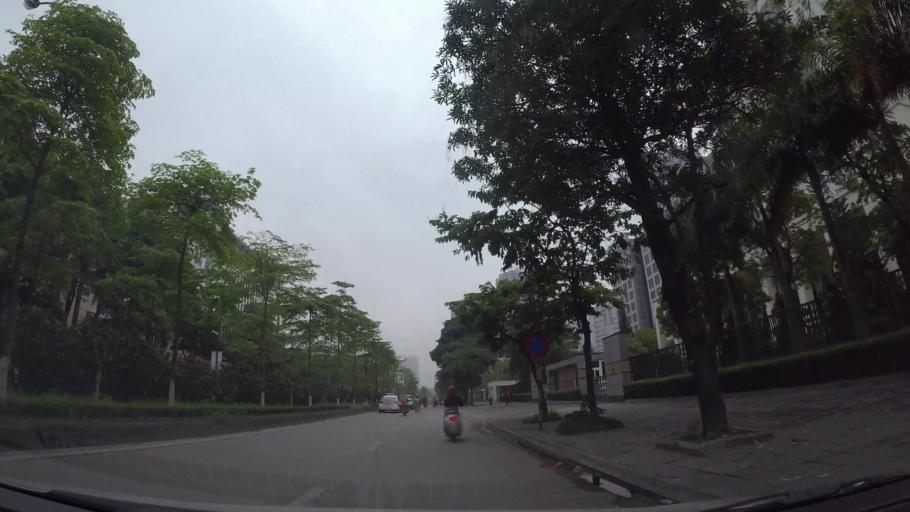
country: VN
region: Ha Noi
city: Cau Giay
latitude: 21.0283
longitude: 105.7822
